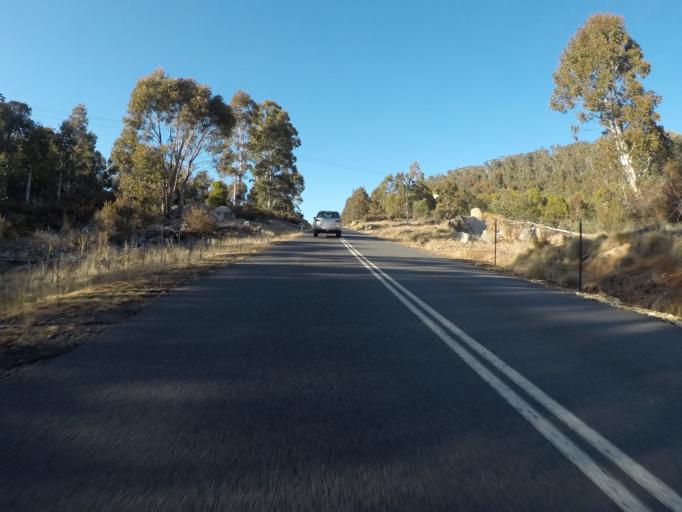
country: AU
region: Australian Capital Territory
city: Macarthur
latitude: -35.5035
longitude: 148.9226
